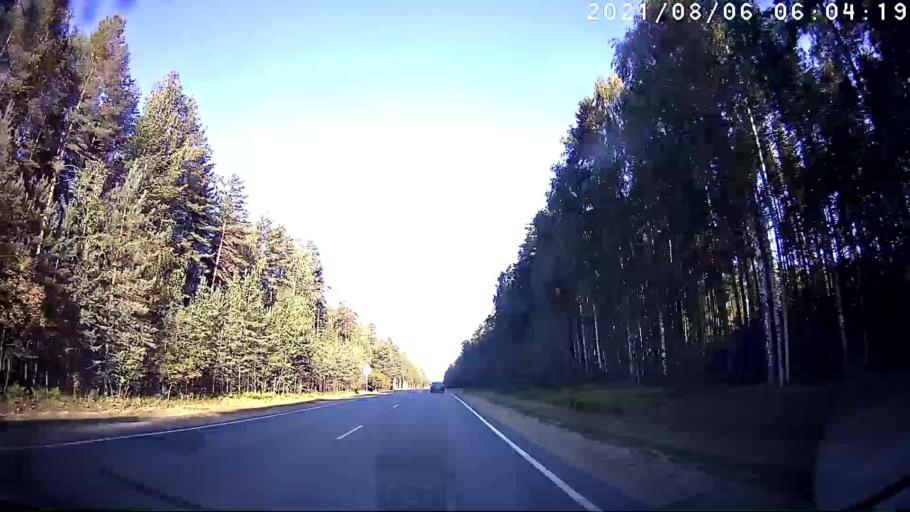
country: RU
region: Mariy-El
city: Privolzhskiy
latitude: 55.8883
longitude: 48.4390
